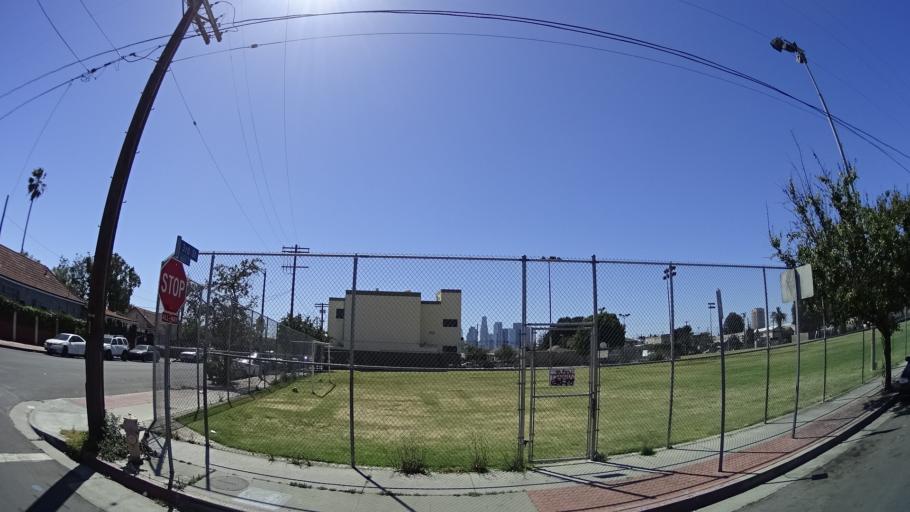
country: US
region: California
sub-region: Los Angeles County
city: Boyle Heights
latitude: 34.0455
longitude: -118.2219
